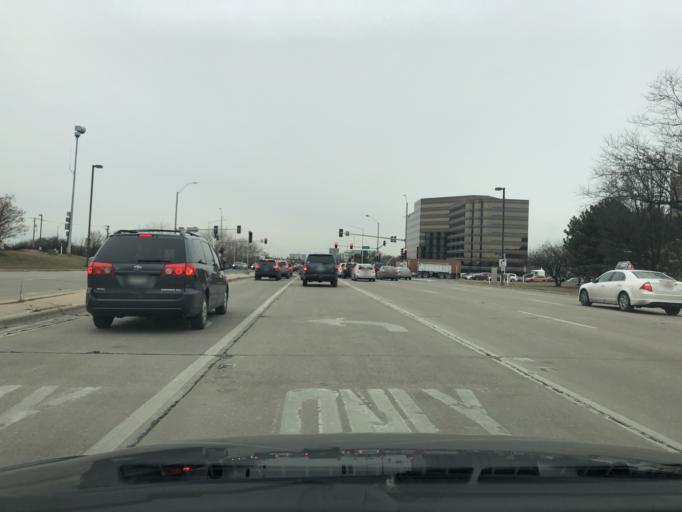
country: US
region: Illinois
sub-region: DuPage County
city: Oakbrook Terrace
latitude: 41.8467
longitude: -87.9564
